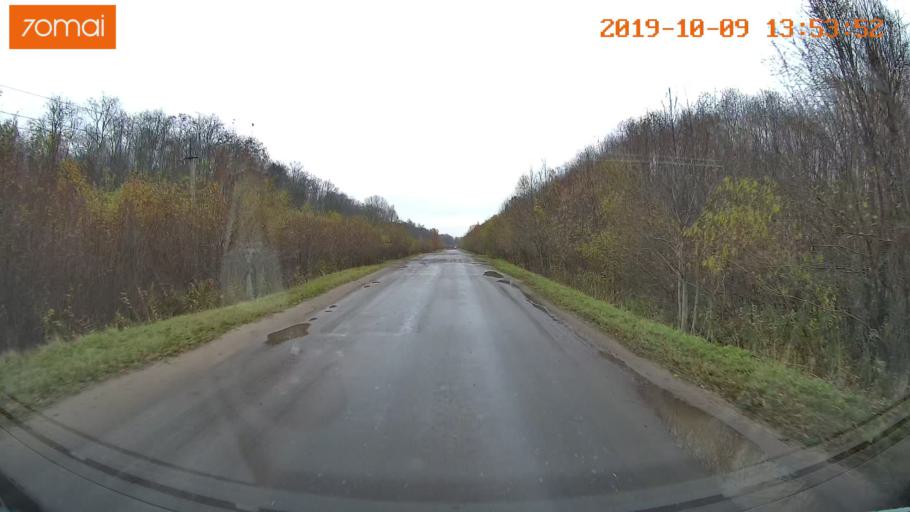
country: RU
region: Kostroma
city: Buy
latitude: 58.4184
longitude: 41.2630
